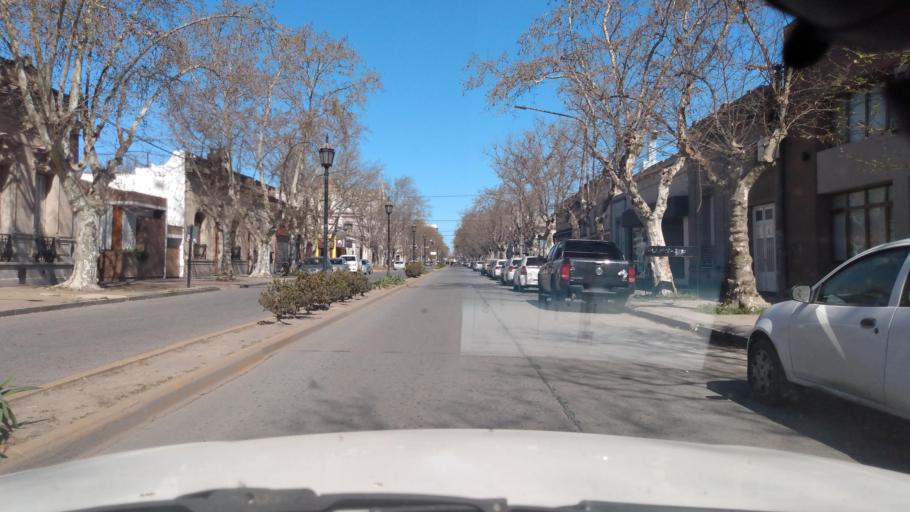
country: AR
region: Buenos Aires
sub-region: Partido de Mercedes
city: Mercedes
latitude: -34.6471
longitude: -59.4309
